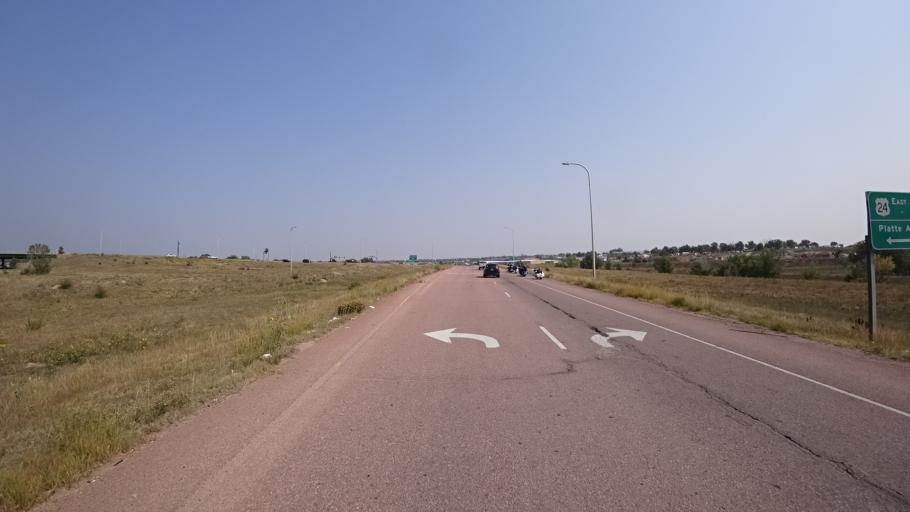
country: US
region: Colorado
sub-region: El Paso County
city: Cimarron Hills
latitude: 38.8368
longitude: -104.7196
